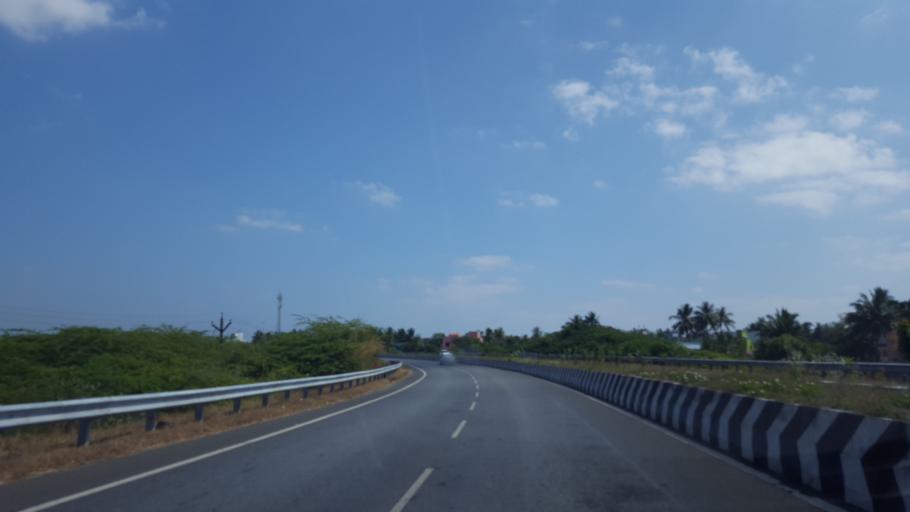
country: IN
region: Tamil Nadu
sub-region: Kancheepuram
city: Mamallapuram
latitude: 12.6236
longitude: 80.1899
